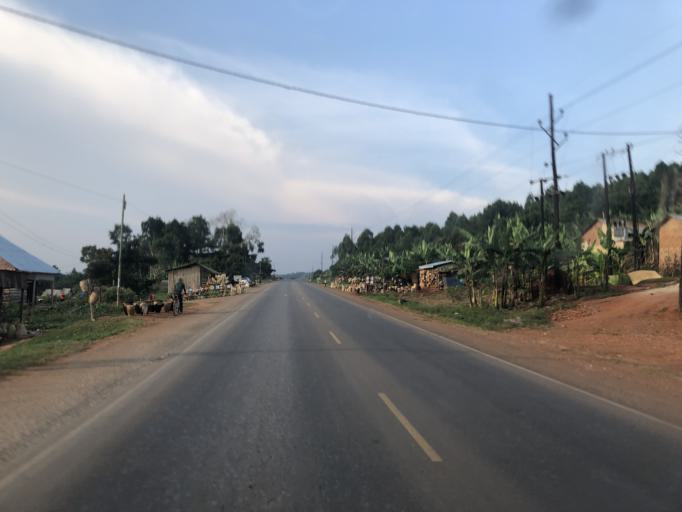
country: UG
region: Central Region
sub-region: Mpigi District
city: Mpigi
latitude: 0.1950
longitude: 32.2969
